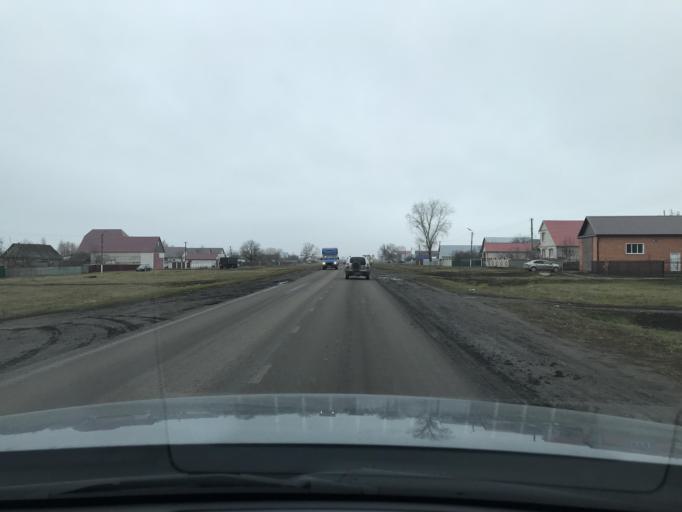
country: RU
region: Penza
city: Zemetchino
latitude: 53.5079
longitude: 42.6373
